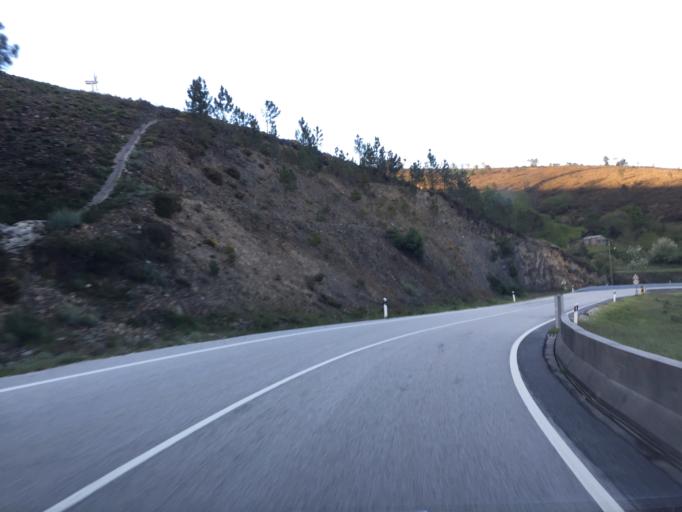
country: PT
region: Coimbra
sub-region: Pampilhosa da Serra
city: Pampilhosa da Serra
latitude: 40.1089
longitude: -8.0109
